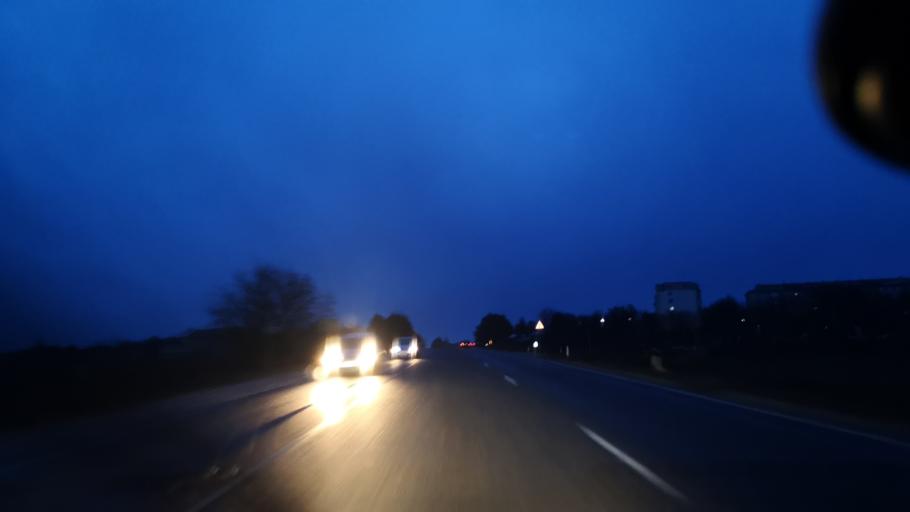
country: MD
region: Orhei
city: Orhei
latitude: 47.3983
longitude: 28.8037
